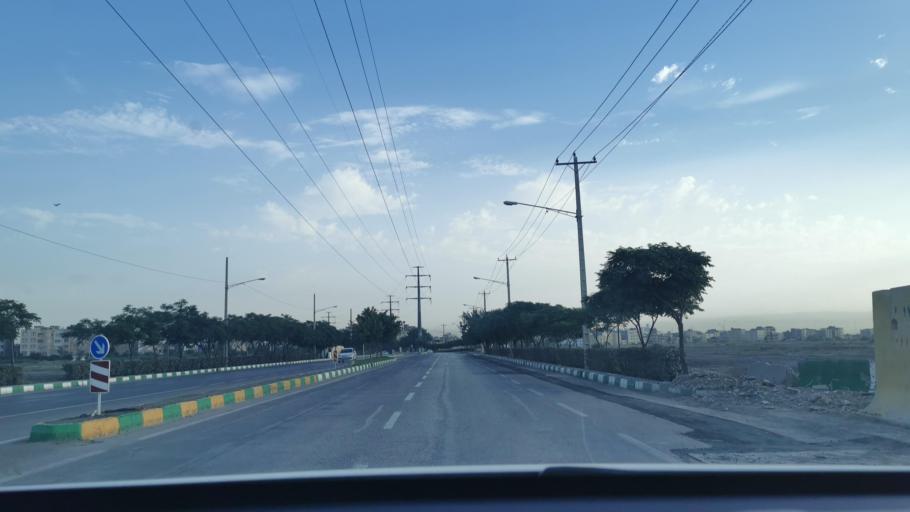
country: IR
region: Razavi Khorasan
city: Mashhad
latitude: 36.3468
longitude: 59.5314
